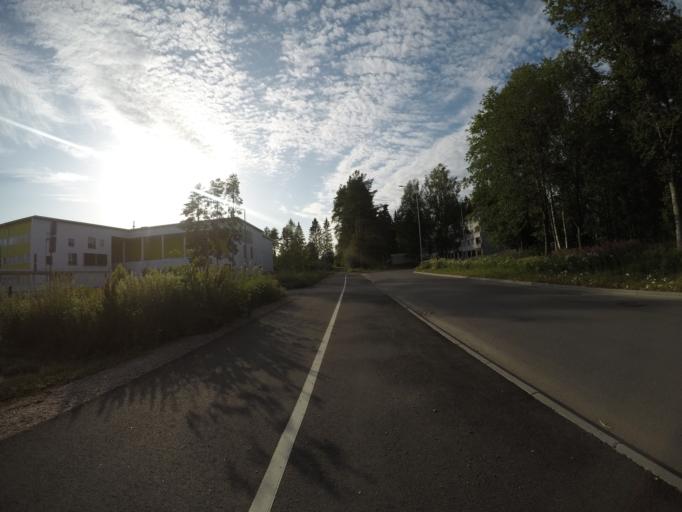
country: FI
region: Haeme
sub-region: Haemeenlinna
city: Haemeenlinna
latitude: 60.9816
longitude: 24.4061
